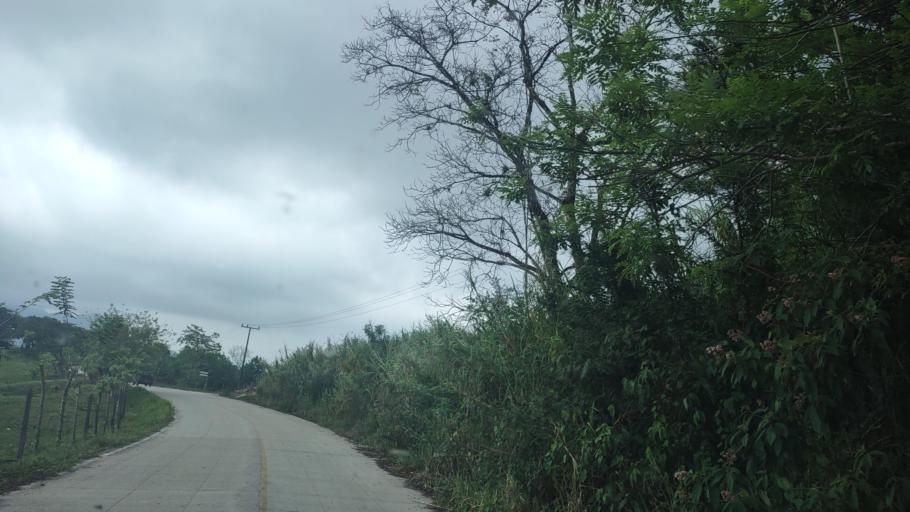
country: MX
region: Veracruz
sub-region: Uxpanapa
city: Poblado 10
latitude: 17.4925
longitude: -94.1762
